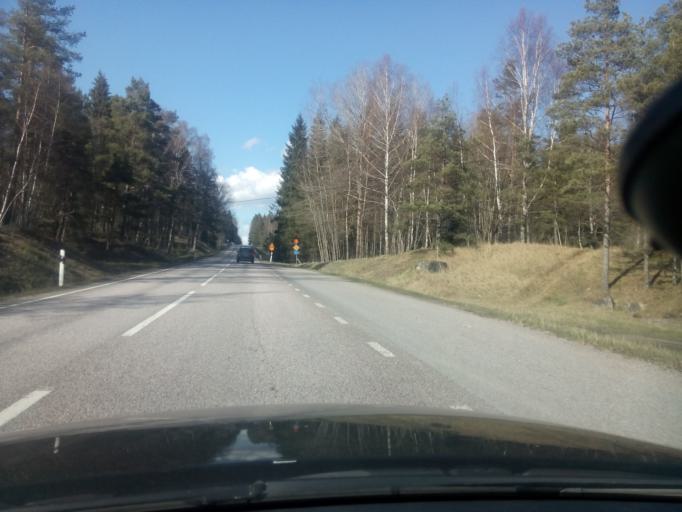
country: SE
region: Soedermanland
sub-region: Strangnas Kommun
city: Akers Styckebruk
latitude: 59.2370
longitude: 16.9375
